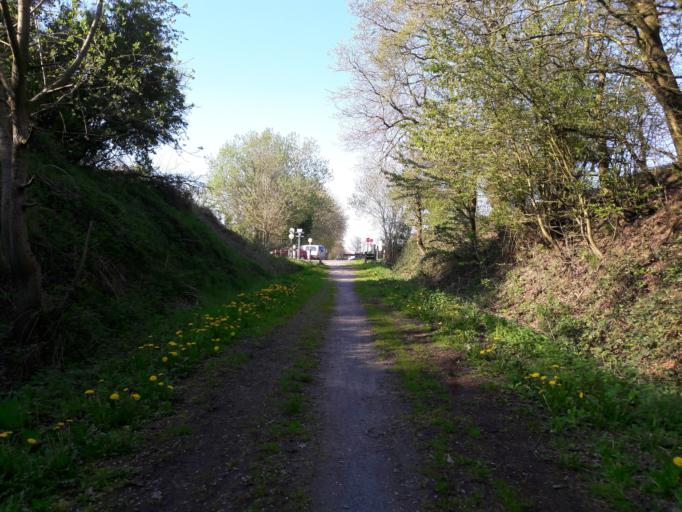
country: FR
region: Nord-Pas-de-Calais
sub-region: Departement du Nord
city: Sains-du-Nord
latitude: 50.1523
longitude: 4.0693
